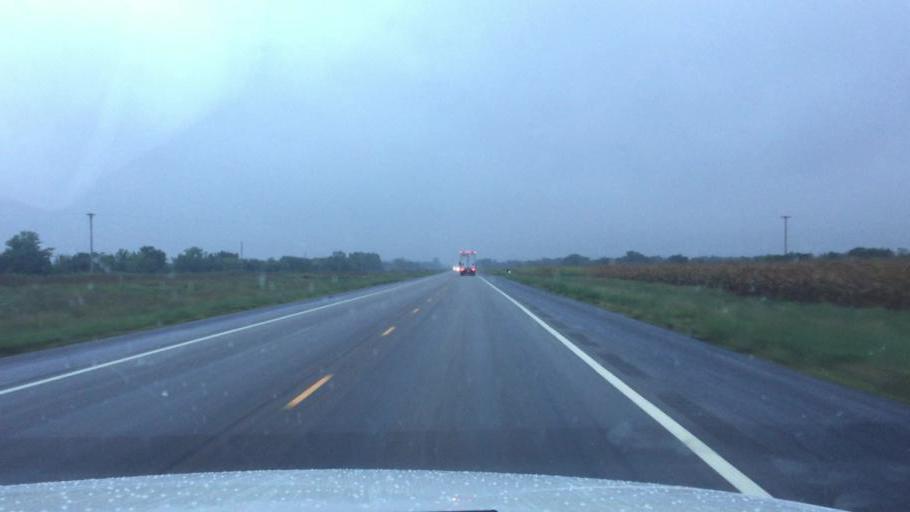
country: US
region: Kansas
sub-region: Montgomery County
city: Cherryvale
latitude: 37.4067
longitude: -95.5010
